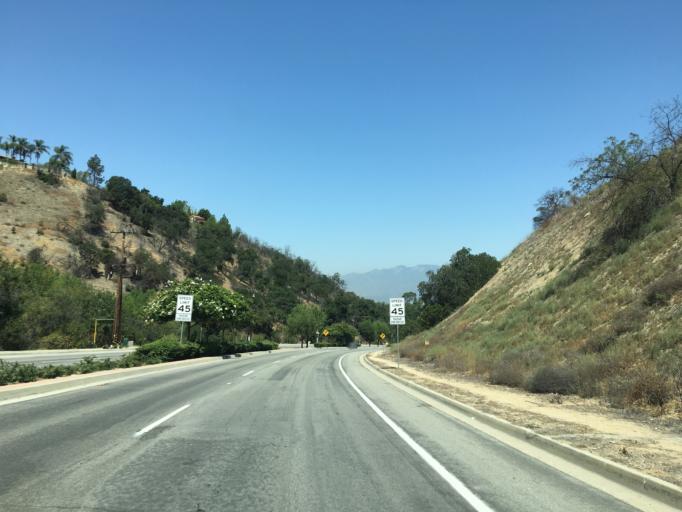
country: US
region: California
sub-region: Los Angeles County
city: Walnut
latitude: 34.0519
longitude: -117.8627
